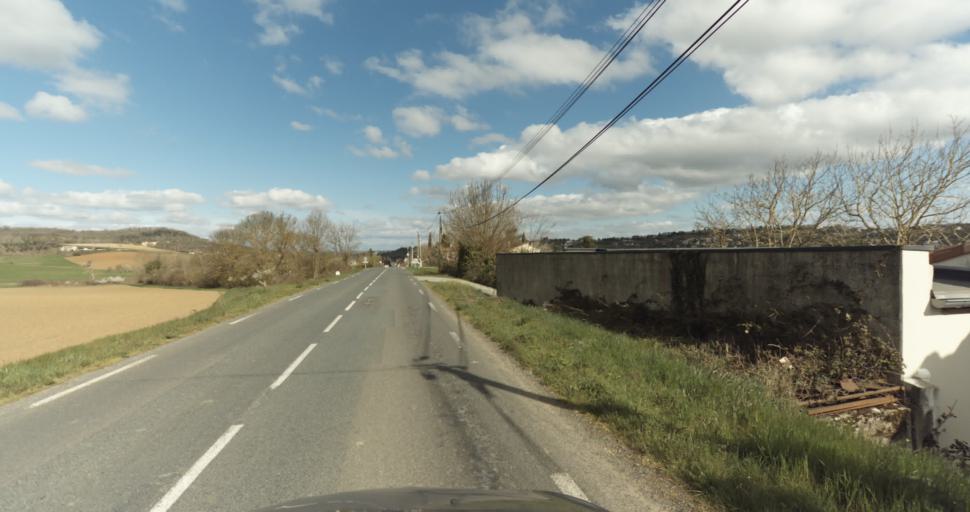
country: FR
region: Midi-Pyrenees
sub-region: Departement du Tarn
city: Puygouzon
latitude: 43.8864
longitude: 2.1542
